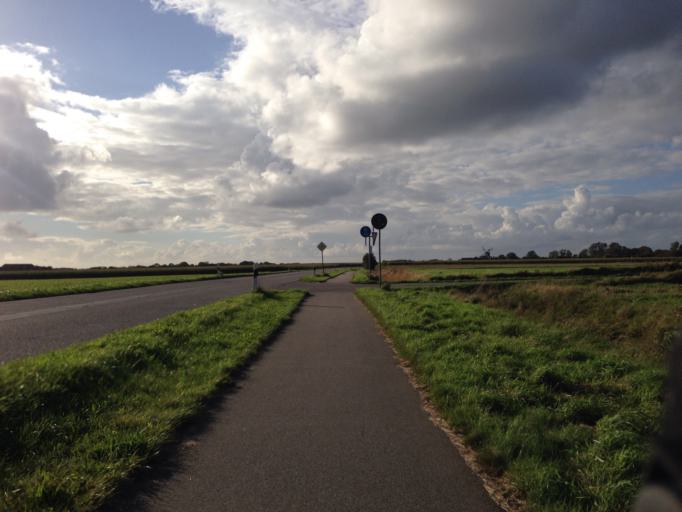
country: DE
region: Schleswig-Holstein
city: Oldsum
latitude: 54.7256
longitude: 8.4616
